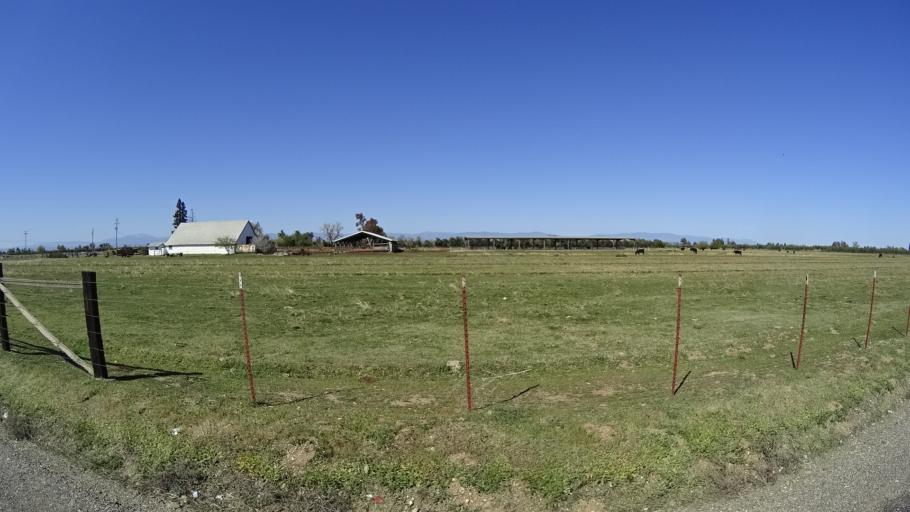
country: US
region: California
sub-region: Glenn County
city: Orland
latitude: 39.7273
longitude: -122.2156
